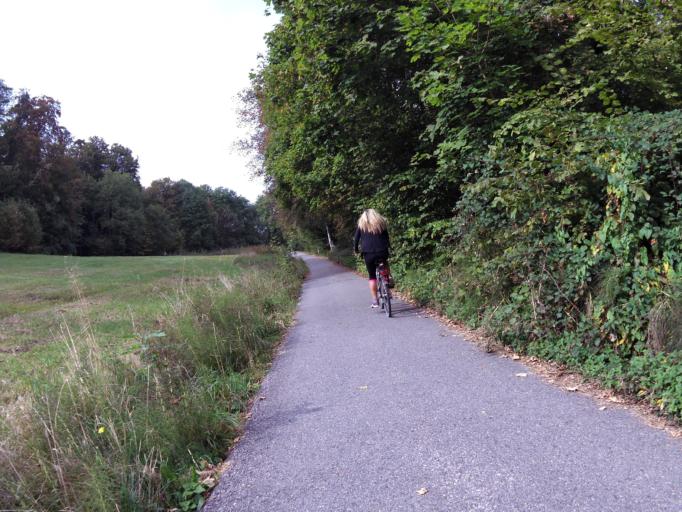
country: DE
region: Bavaria
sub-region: Upper Bavaria
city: Bernried
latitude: 47.8640
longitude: 11.2990
